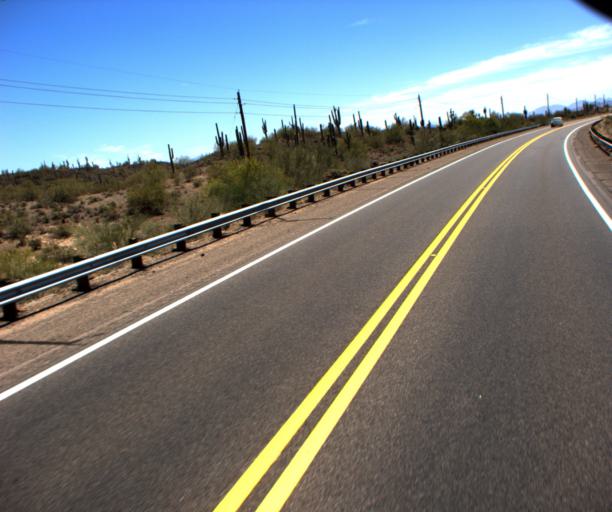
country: US
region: Arizona
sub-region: Maricopa County
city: Anthem
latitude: 33.8337
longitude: -112.3064
